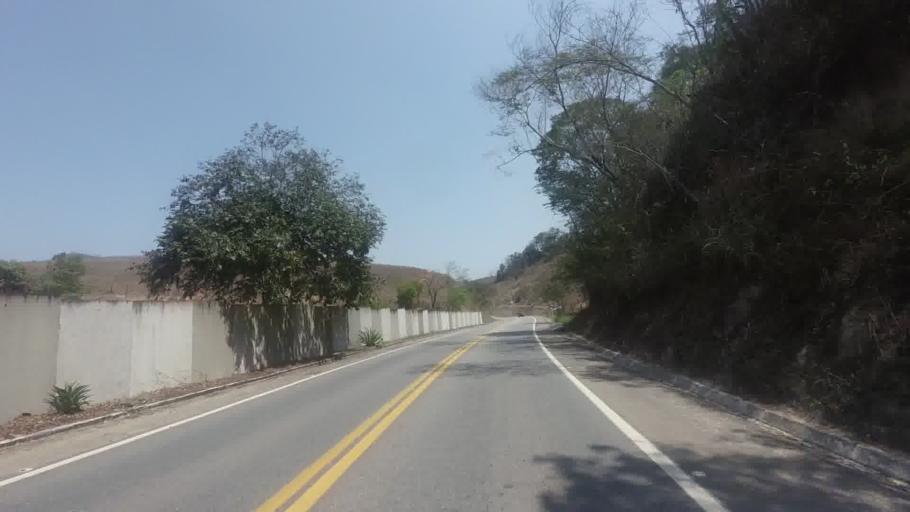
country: BR
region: Espirito Santo
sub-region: Mimoso Do Sul
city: Mimoso do Sul
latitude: -20.9320
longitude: -41.3217
